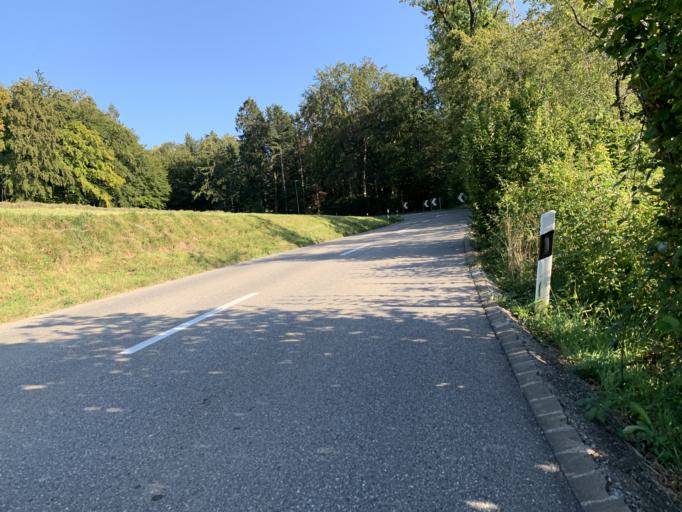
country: CH
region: Zurich
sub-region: Bezirk Hinwil
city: Hinwil
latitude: 47.2997
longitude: 8.8541
